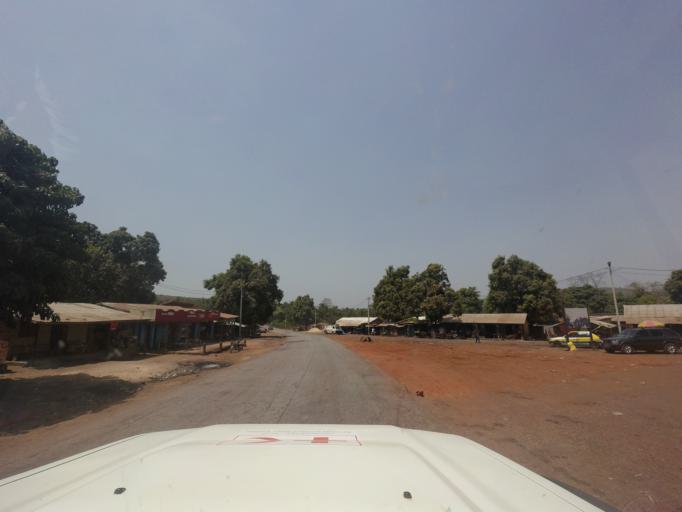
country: GN
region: Kindia
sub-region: Kindia
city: Kindia
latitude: 9.8604
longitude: -13.0812
